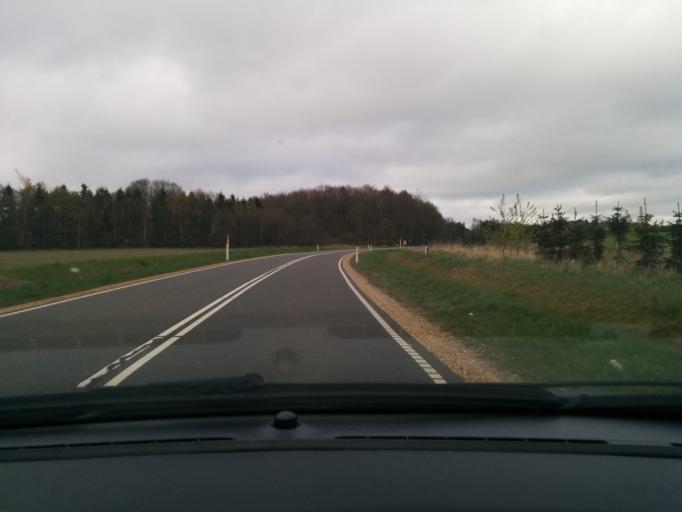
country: DK
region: Central Jutland
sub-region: Silkeborg Kommune
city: Svejbaek
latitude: 56.1985
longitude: 9.7071
